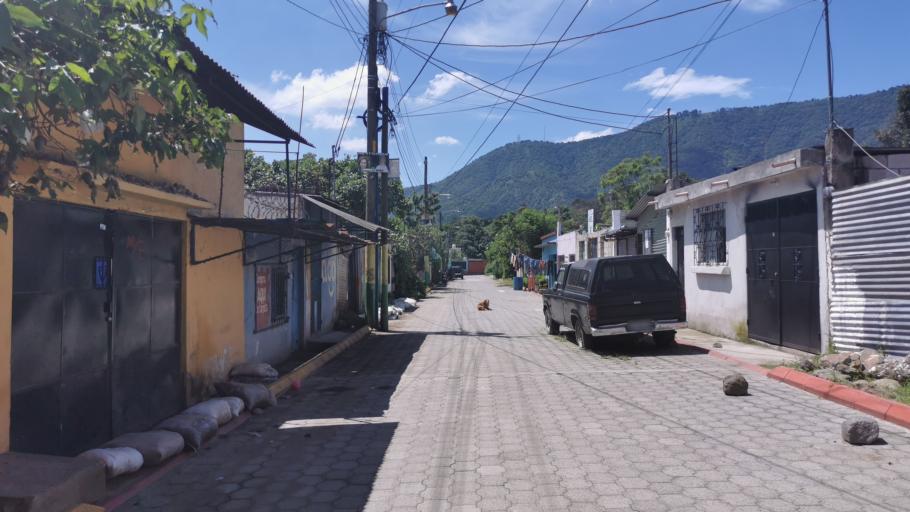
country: GT
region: Guatemala
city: Amatitlan
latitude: 14.4861
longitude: -90.6400
